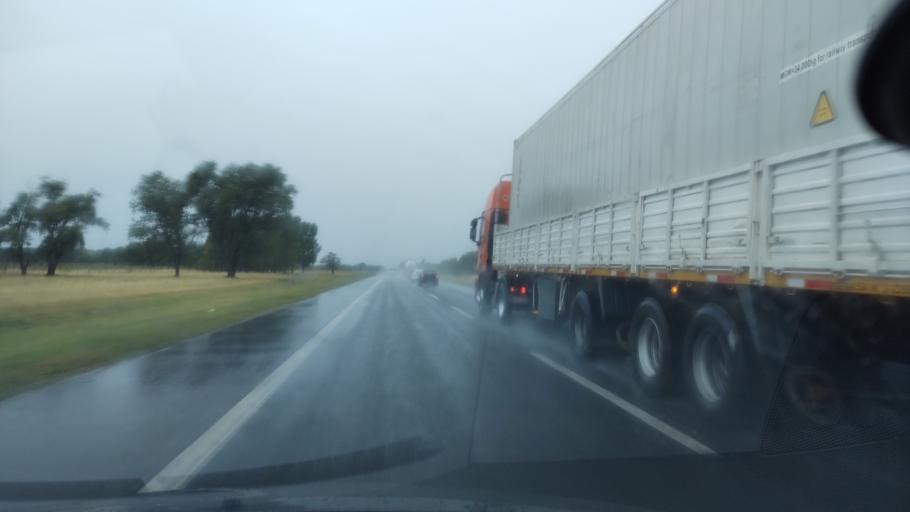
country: AR
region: Buenos Aires
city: Canuelas
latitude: -35.0625
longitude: -58.8138
